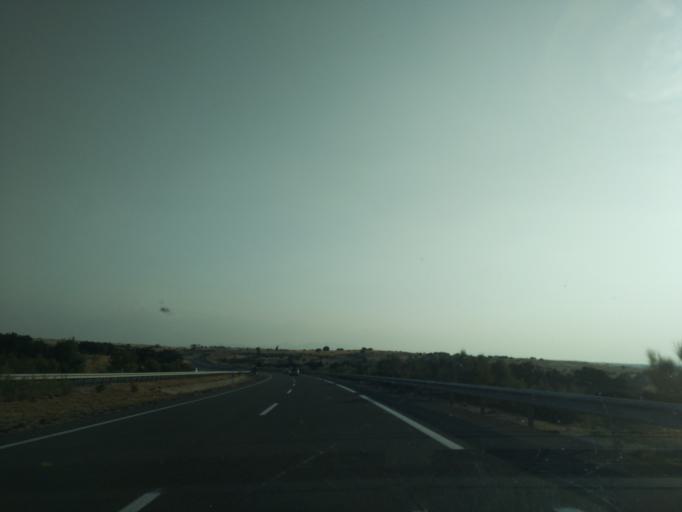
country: ES
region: Castille and Leon
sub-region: Provincia de Avila
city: Mediana de Voltoya
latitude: 40.7116
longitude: -4.5586
